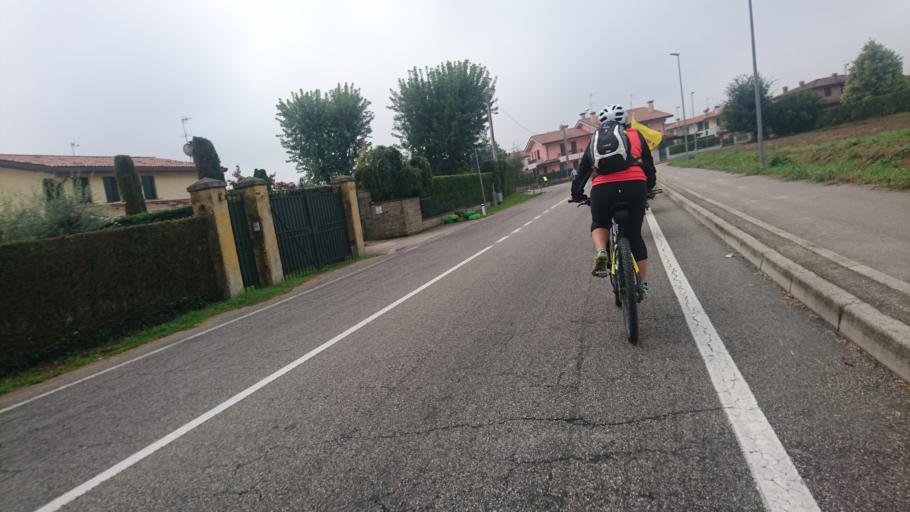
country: IT
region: Veneto
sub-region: Provincia di Padova
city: Monselice
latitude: 45.2349
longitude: 11.7659
